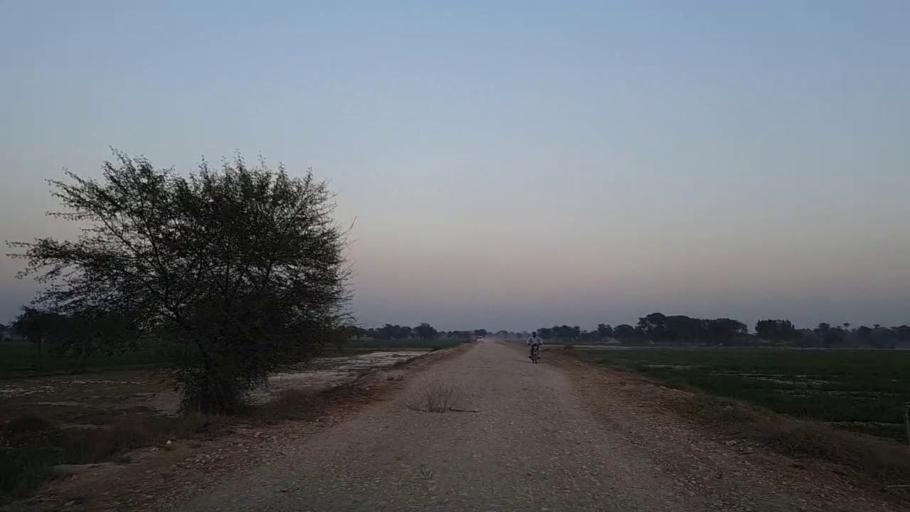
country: PK
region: Sindh
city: Naushahro Firoz
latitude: 26.8005
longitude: 68.0164
